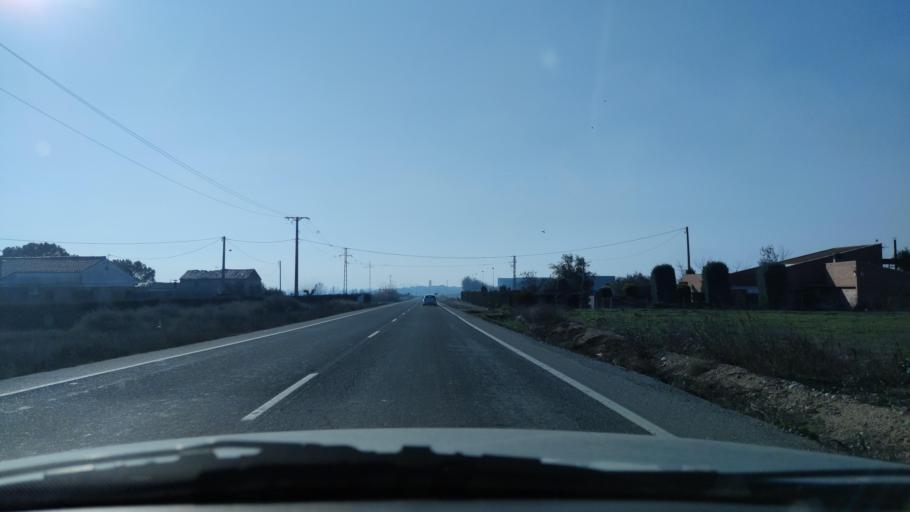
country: ES
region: Catalonia
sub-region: Provincia de Lleida
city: Torrefarrera
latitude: 41.6853
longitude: 0.6325
